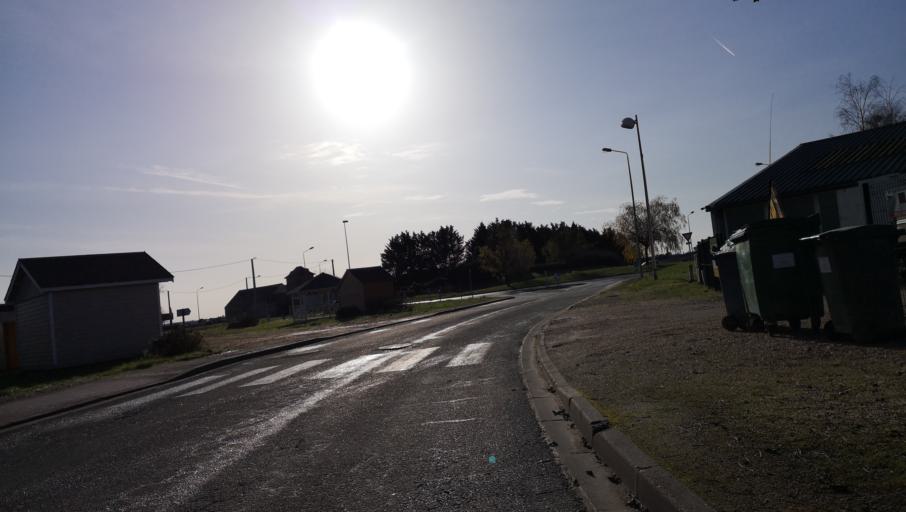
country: FR
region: Centre
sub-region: Departement du Loiret
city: Saint-Denis-en-Val
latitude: 47.8756
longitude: 1.9450
